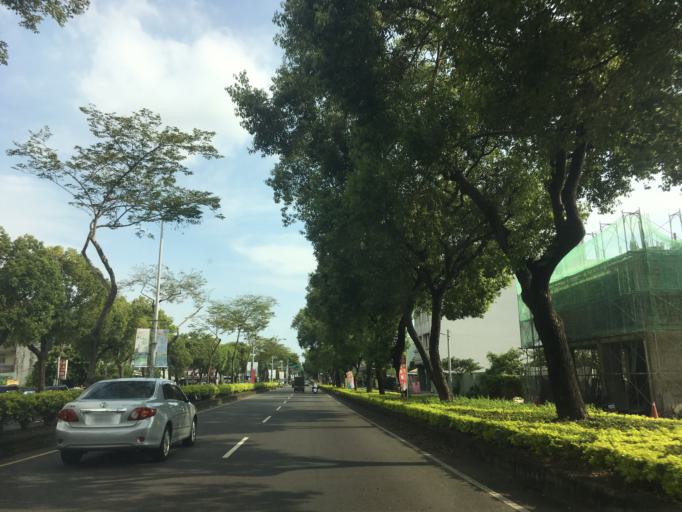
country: TW
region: Taiwan
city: Zhongxing New Village
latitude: 23.9825
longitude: 120.6814
